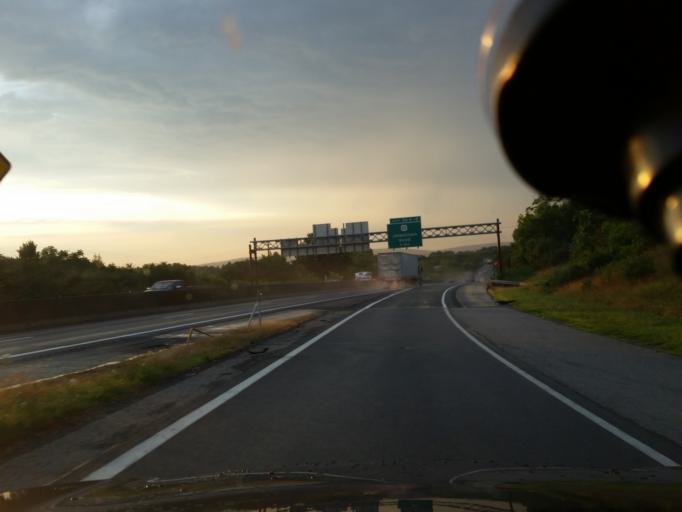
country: US
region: Pennsylvania
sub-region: Dauphin County
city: Progress
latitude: 40.2805
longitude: -76.8193
